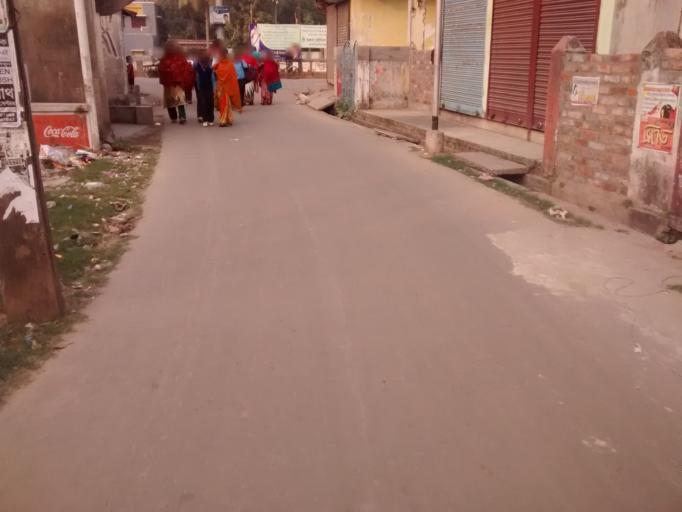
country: IN
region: West Bengal
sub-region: North 24 Parganas
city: Barasat
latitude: 22.7192
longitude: 88.4693
